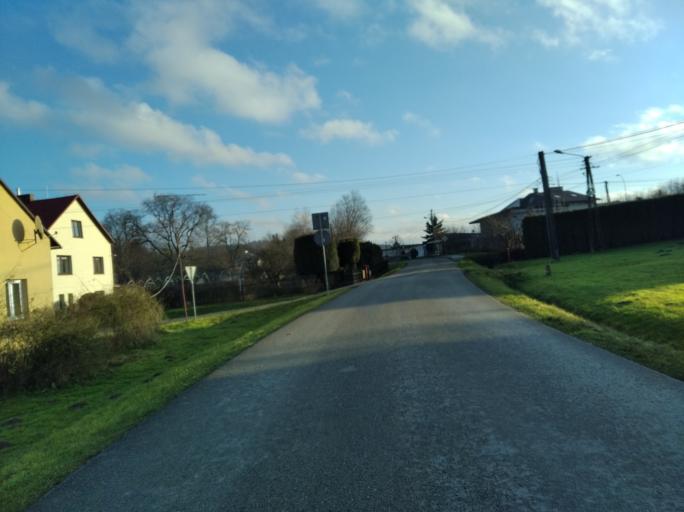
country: PL
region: Subcarpathian Voivodeship
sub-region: Powiat strzyzowski
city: Czudec
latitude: 49.9418
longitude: 21.8116
